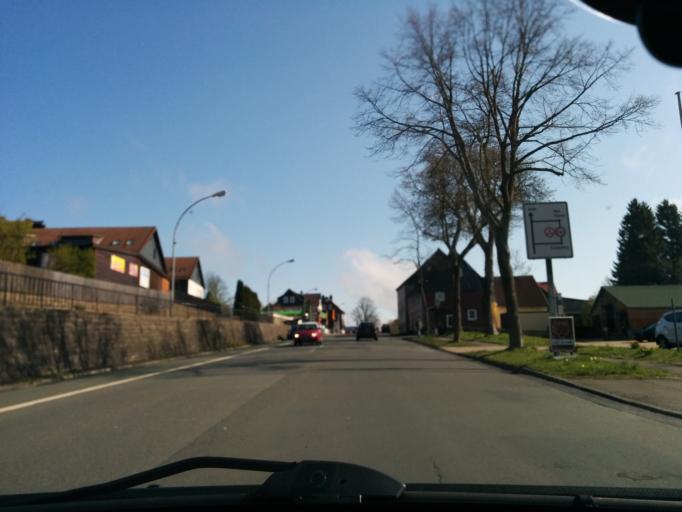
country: DE
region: Lower Saxony
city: Clausthal-Zellerfeld
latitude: 51.8195
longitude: 10.3394
